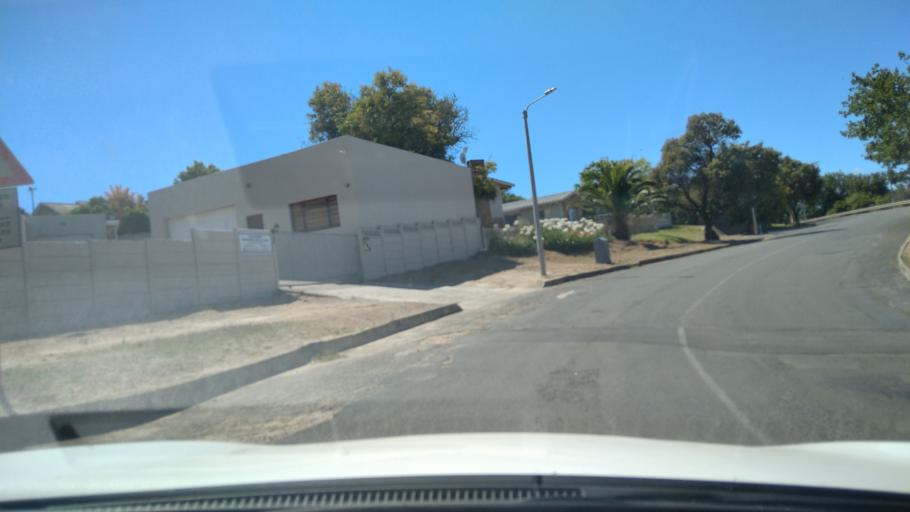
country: ZA
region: Western Cape
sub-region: Overberg District Municipality
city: Caledon
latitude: -34.2288
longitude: 19.4305
